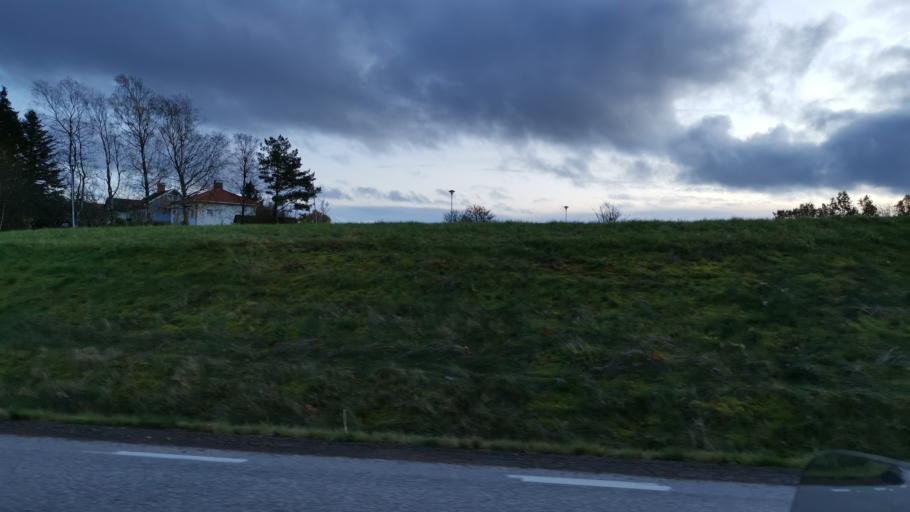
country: SE
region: Vaestra Goetaland
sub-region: Munkedals Kommun
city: Munkedal
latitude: 58.4739
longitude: 11.6659
